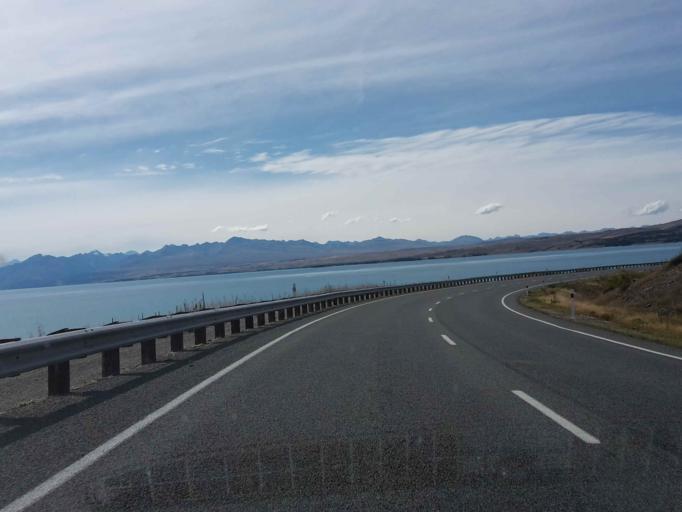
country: NZ
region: Canterbury
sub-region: Timaru District
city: Pleasant Point
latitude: -44.1772
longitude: 170.1563
